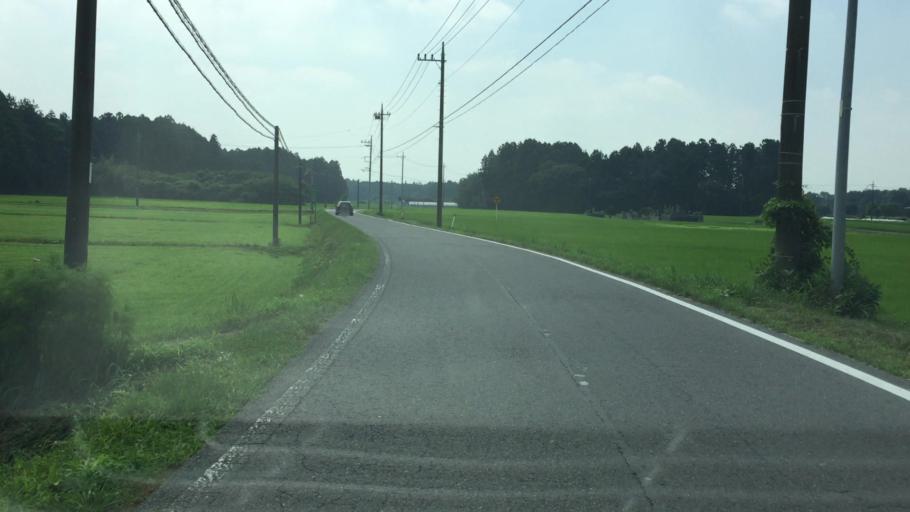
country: JP
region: Tochigi
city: Kuroiso
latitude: 36.9609
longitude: 139.9523
